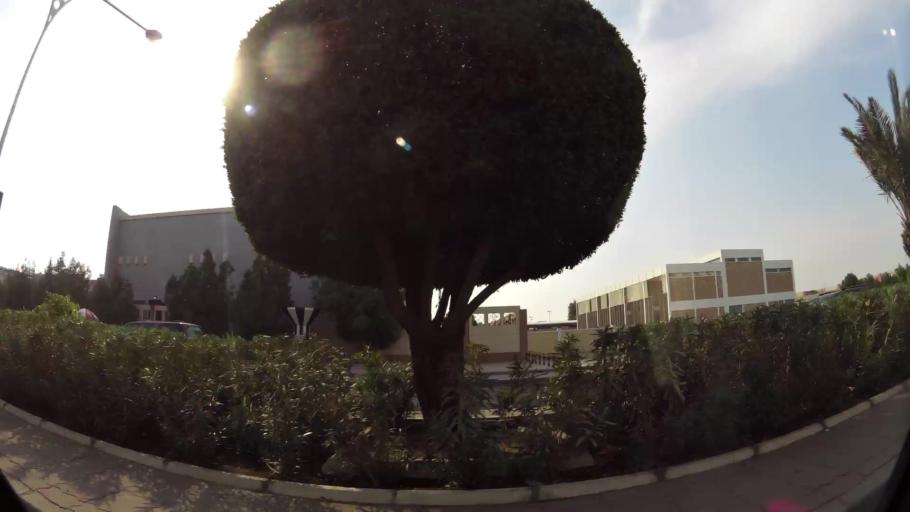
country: KW
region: Al Farwaniyah
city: Janub as Surrah
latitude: 29.3120
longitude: 47.9888
